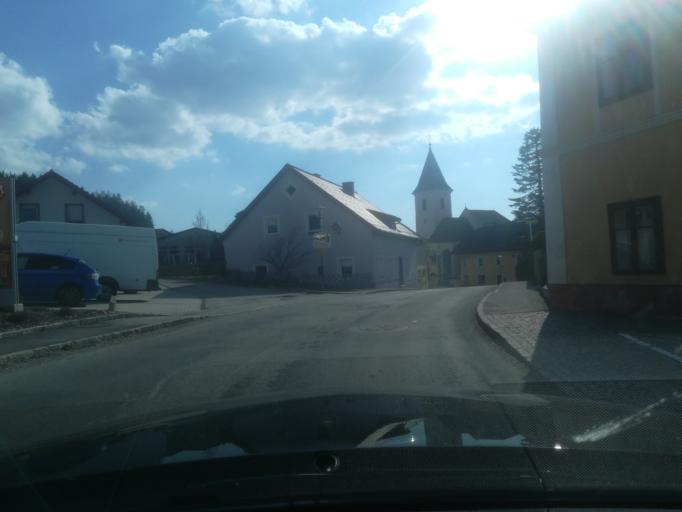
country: AT
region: Upper Austria
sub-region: Politischer Bezirk Freistadt
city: Freistadt
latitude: 48.4447
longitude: 14.6789
